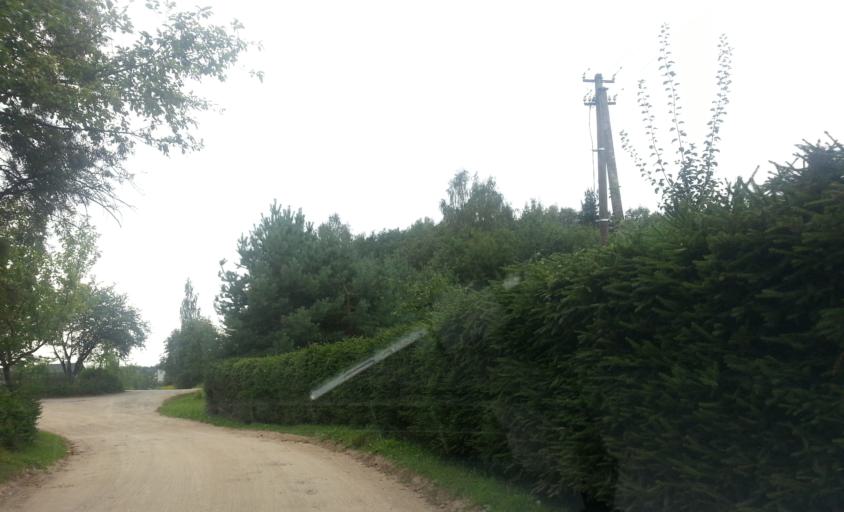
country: LT
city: Grigiskes
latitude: 54.7581
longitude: 25.0207
